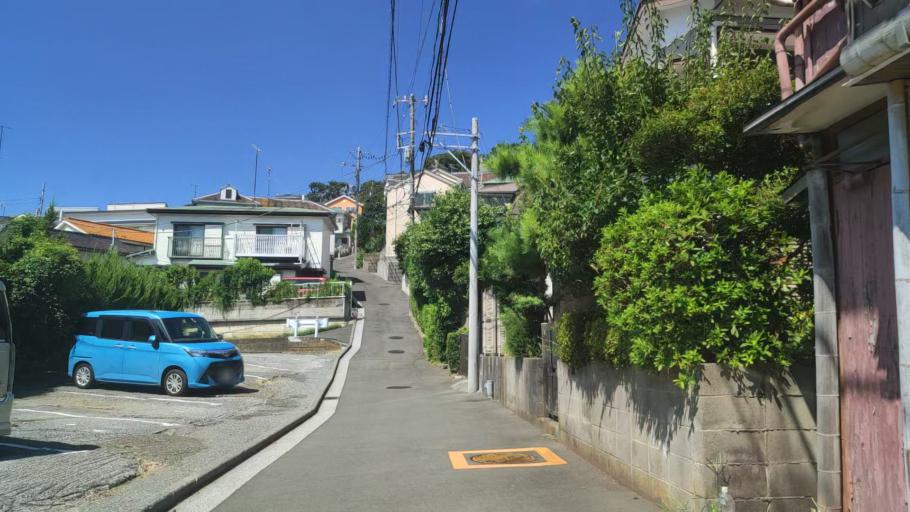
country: JP
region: Kanagawa
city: Yokohama
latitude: 35.5144
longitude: 139.6412
